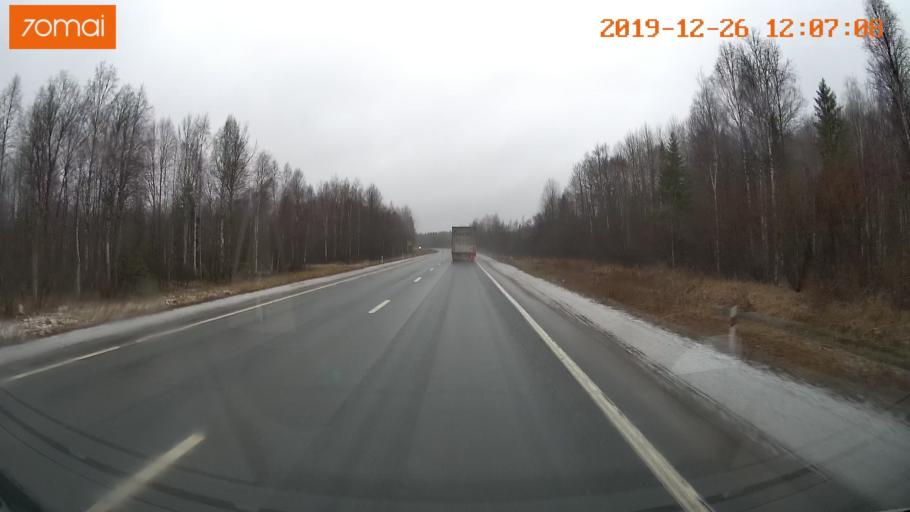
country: RU
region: Vologda
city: Tonshalovo
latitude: 59.2912
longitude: 38.0390
